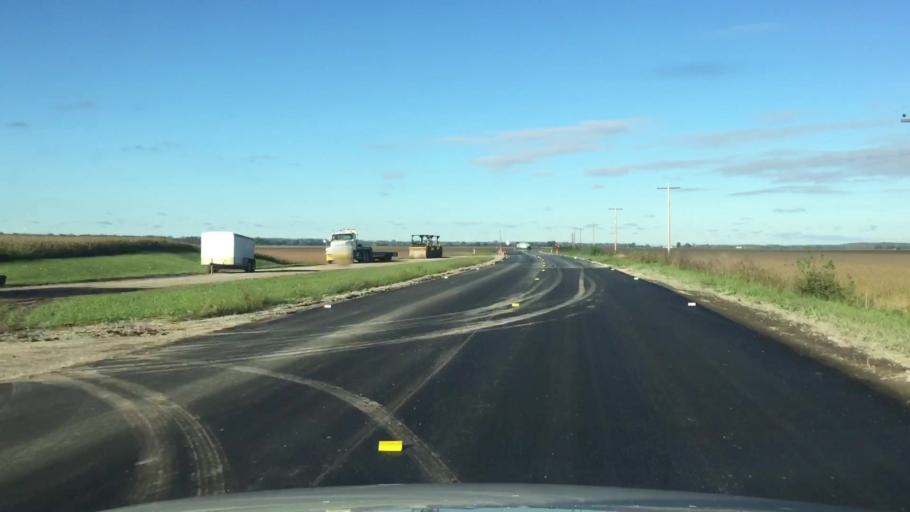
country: US
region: Missouri
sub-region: Howard County
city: New Franklin
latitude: 38.9917
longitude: -92.6205
